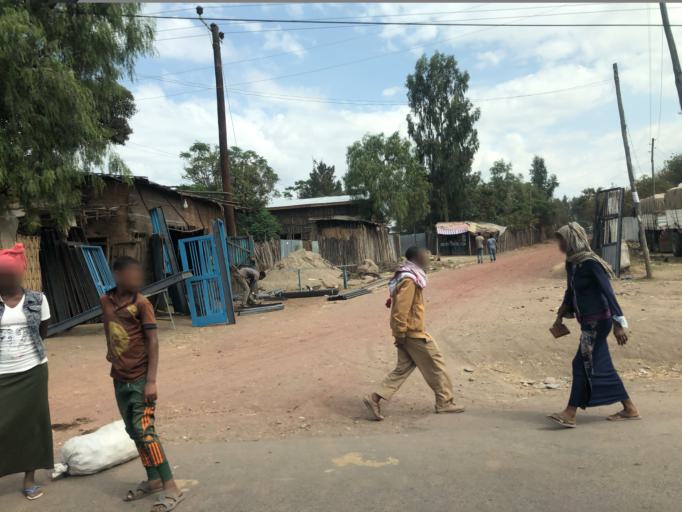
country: ET
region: Oromiya
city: Shashemene
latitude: 7.3658
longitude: 38.6713
